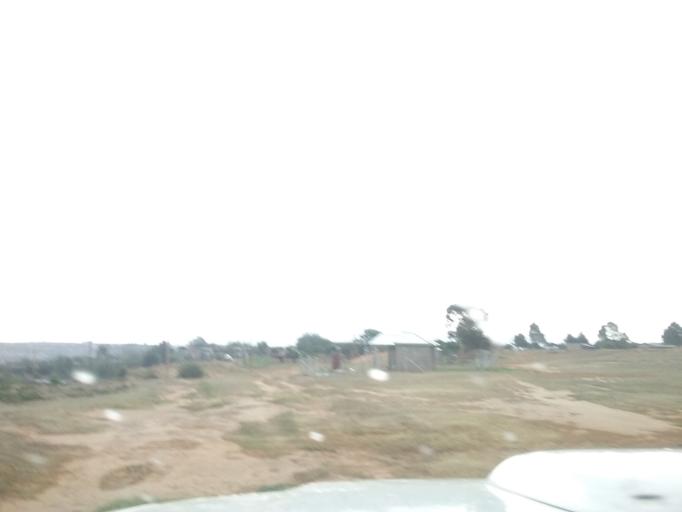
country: LS
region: Maseru
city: Maseru
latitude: -29.4323
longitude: 27.5729
